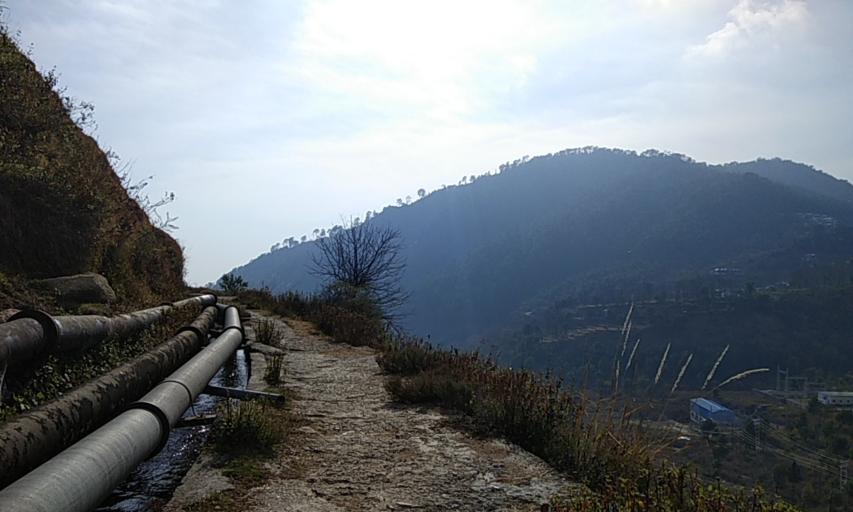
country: IN
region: Himachal Pradesh
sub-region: Kangra
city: Palampur
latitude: 32.1448
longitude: 76.5403
